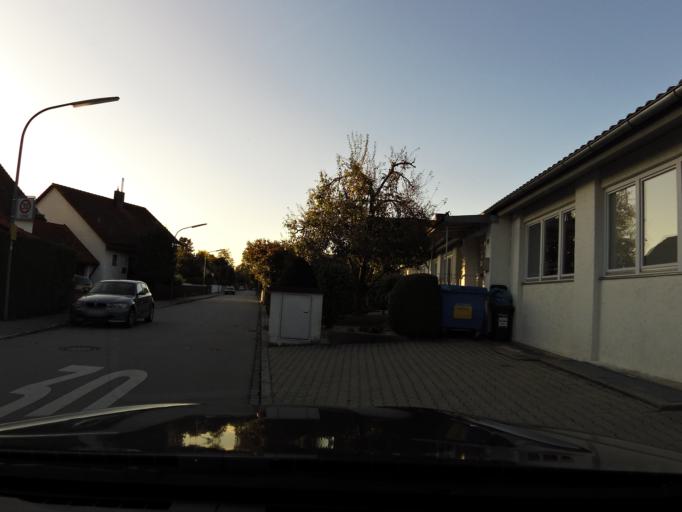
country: DE
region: Bavaria
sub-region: Lower Bavaria
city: Landshut
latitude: 48.5476
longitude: 12.1712
